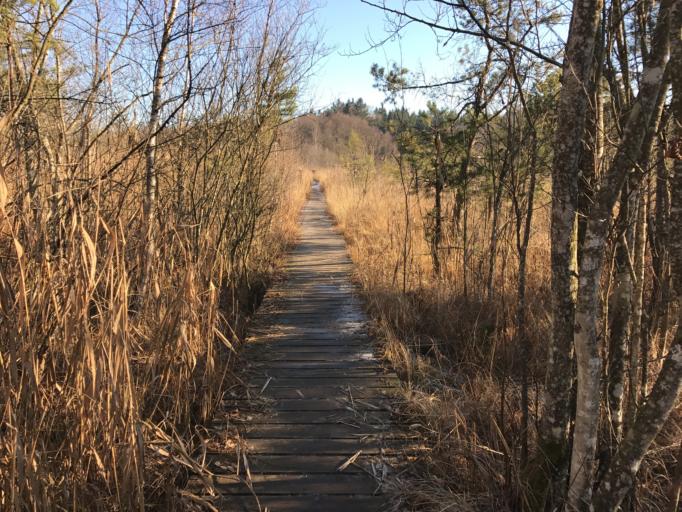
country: DE
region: Bavaria
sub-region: Upper Bavaria
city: Prutting
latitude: 47.8944
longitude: 12.1596
